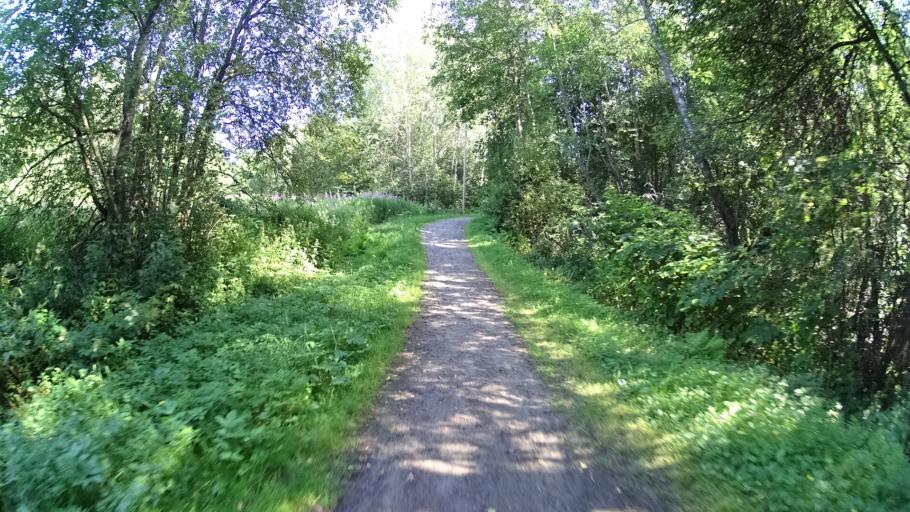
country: FI
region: Uusimaa
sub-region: Helsinki
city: Espoo
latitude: 60.2254
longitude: 24.6617
